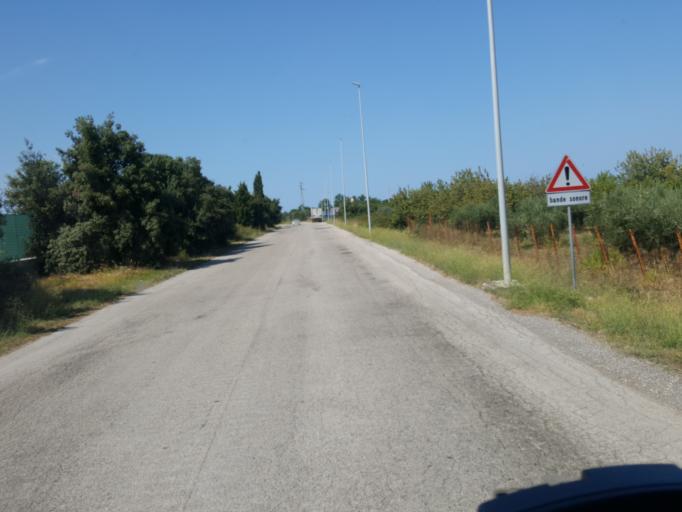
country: IT
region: Abruzzo
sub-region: Provincia di Chieti
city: Salvo Marina
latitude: 42.0637
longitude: 14.7623
